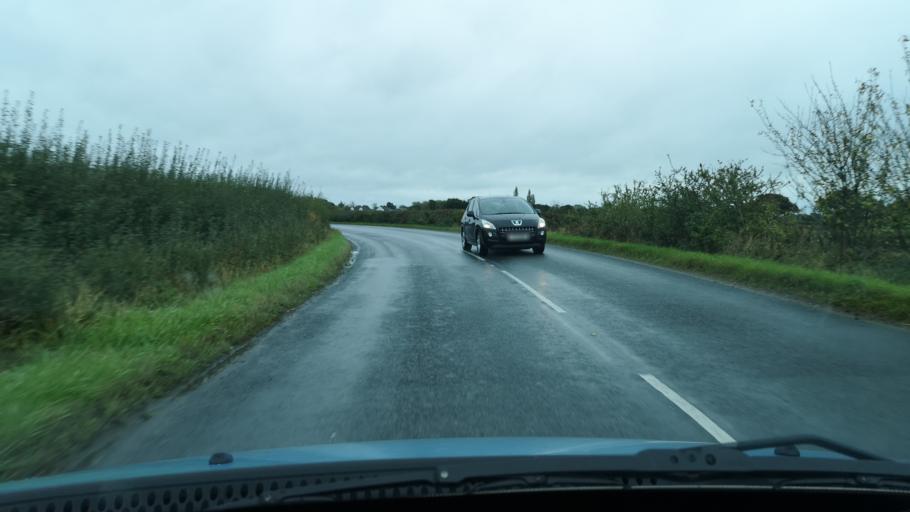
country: GB
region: England
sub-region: Doncaster
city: Moss
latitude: 53.6207
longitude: -1.1249
